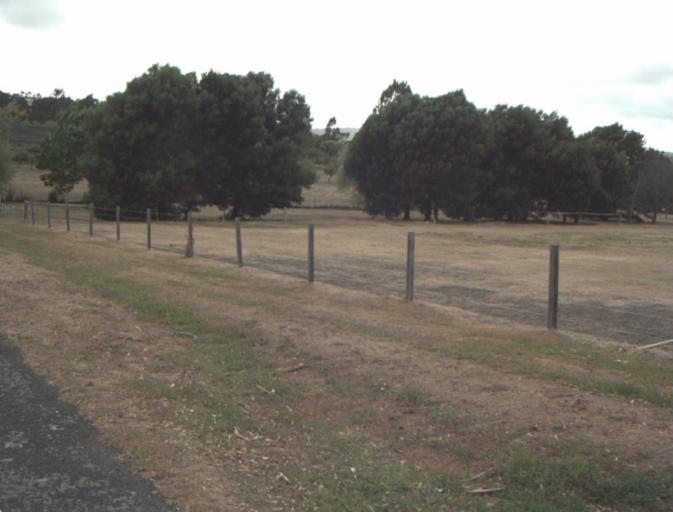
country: AU
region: Tasmania
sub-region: Launceston
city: Mayfield
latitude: -41.3307
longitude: 147.0567
